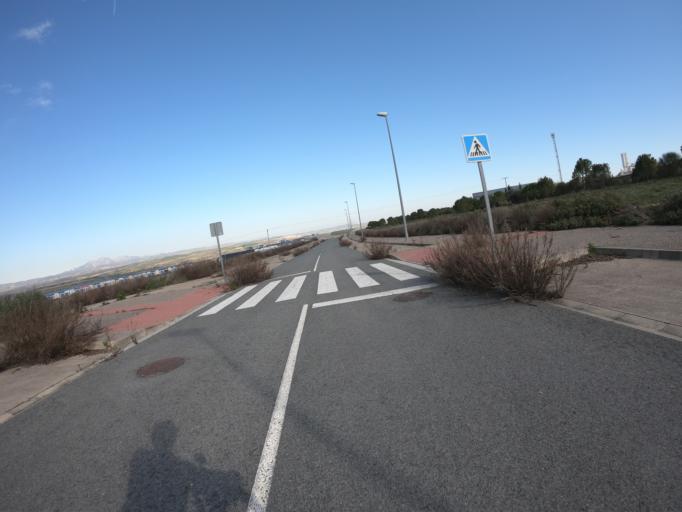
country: ES
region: Basque Country
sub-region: Provincia de Alava
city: Oyon
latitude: 42.4862
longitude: -2.4300
